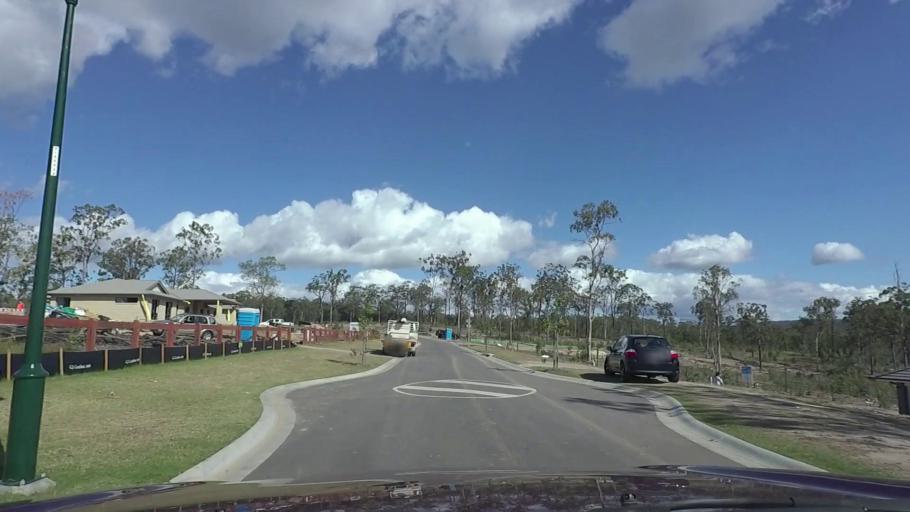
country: AU
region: Queensland
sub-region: Ipswich
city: Springfield Lakes
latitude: -27.7553
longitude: 152.9207
